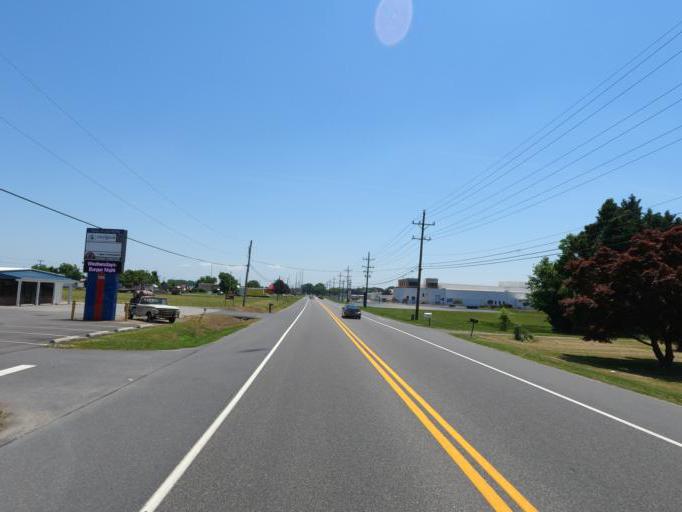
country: US
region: Delaware
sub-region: Sussex County
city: Milford
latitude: 38.9224
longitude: -75.4527
